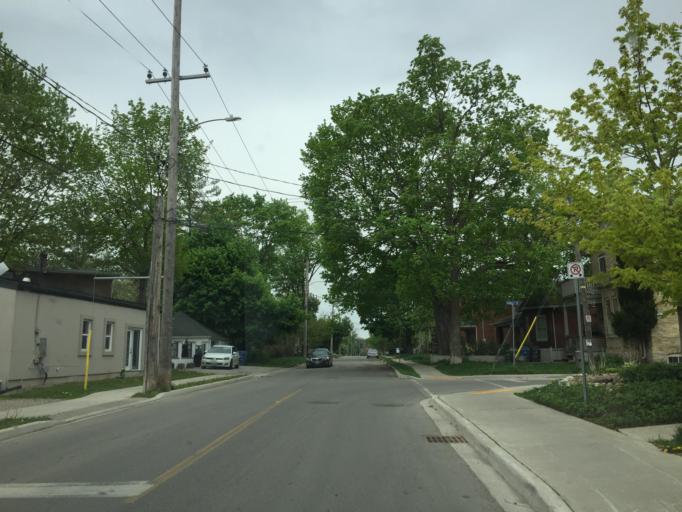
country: CA
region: Ontario
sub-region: Wellington County
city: Guelph
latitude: 43.5441
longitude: -80.2404
